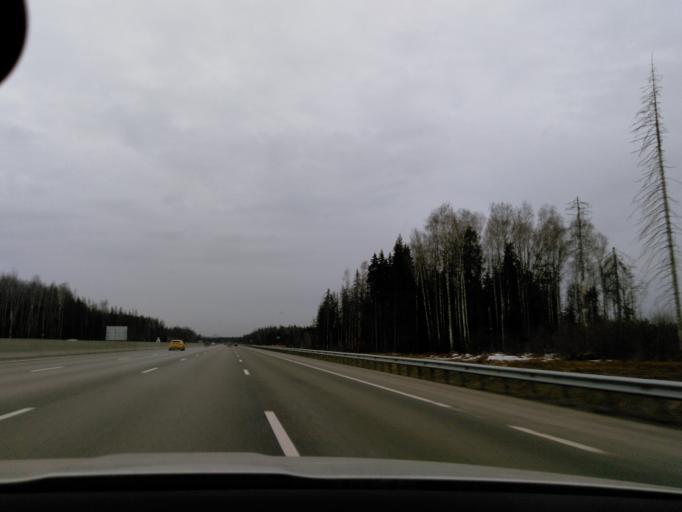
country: RU
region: Moskovskaya
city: Rzhavki
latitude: 56.0013
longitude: 37.2940
